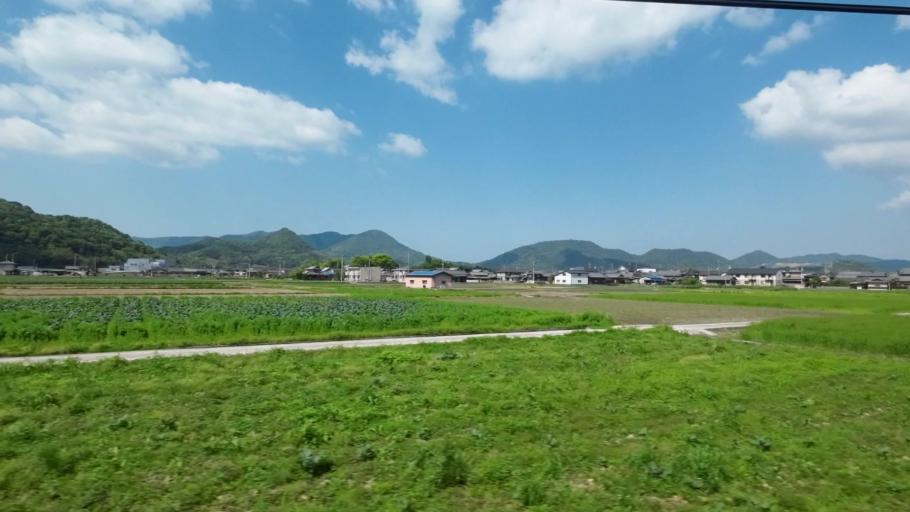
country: JP
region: Kagawa
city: Tadotsu
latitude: 34.2026
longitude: 133.7119
